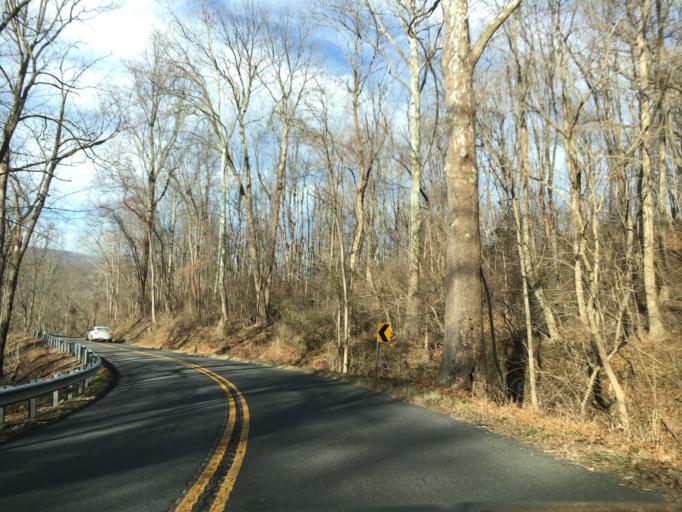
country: US
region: Virginia
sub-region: Warren County
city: Apple Mountain Lake
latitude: 38.8892
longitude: -78.0013
